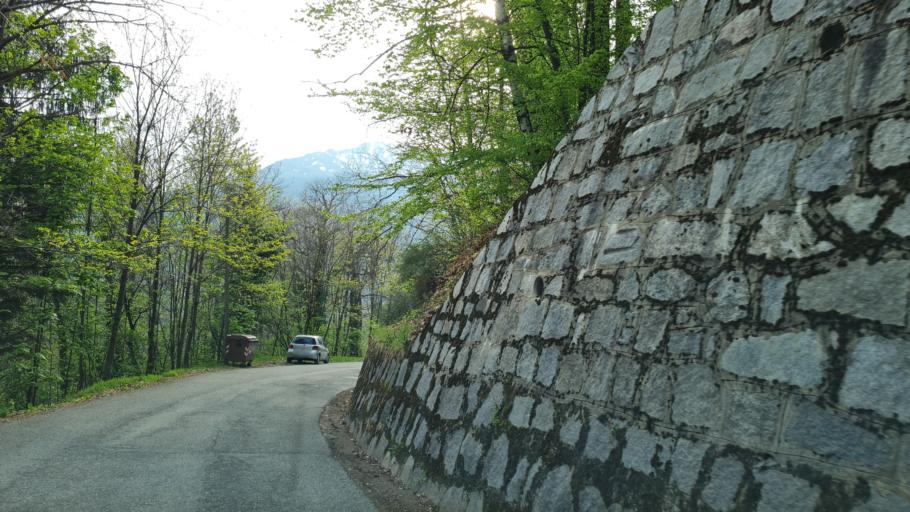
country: IT
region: Piedmont
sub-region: Provincia di Biella
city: Sordevolo
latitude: 45.5780
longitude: 7.9743
